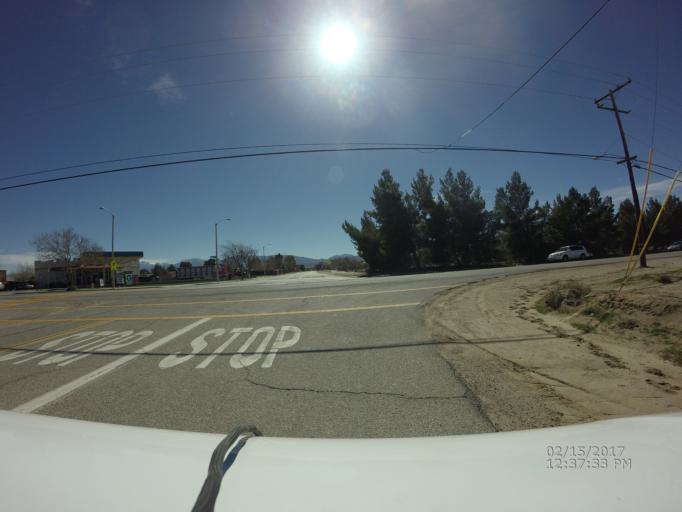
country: US
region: California
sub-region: Los Angeles County
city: Littlerock
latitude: 34.5799
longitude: -117.9607
